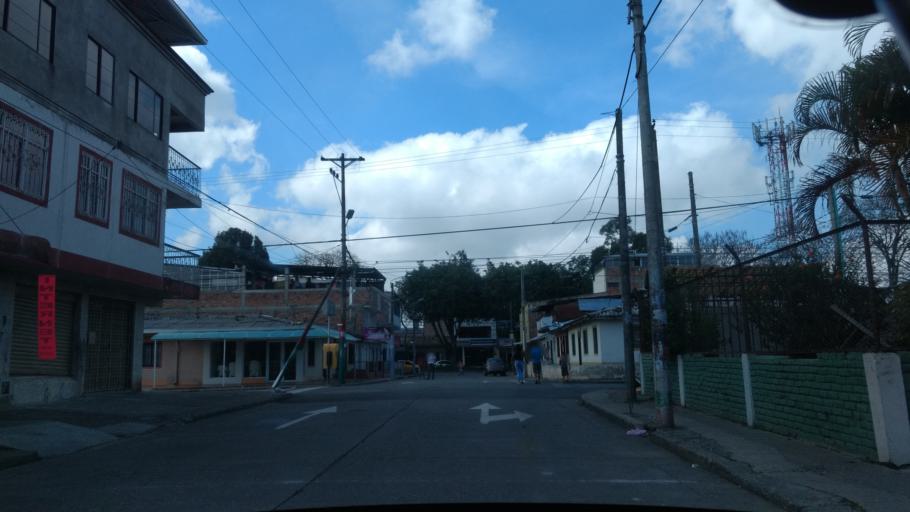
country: CO
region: Cauca
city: Popayan
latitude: 2.4468
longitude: -76.6161
